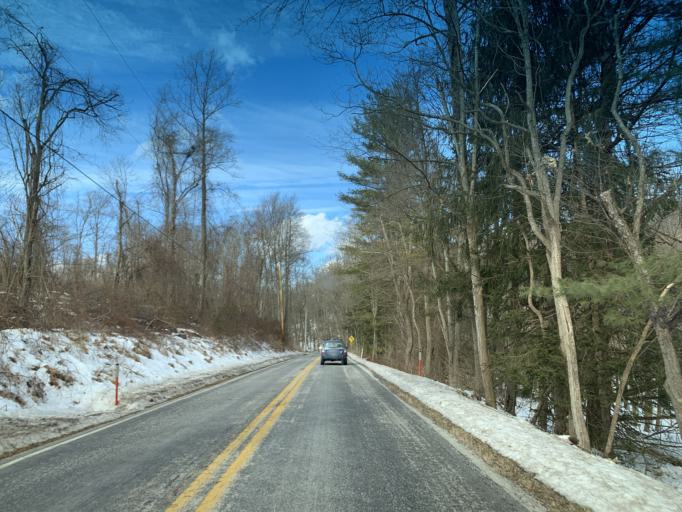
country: US
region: Pennsylvania
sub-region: York County
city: Shrewsbury
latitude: 39.8015
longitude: -76.6560
